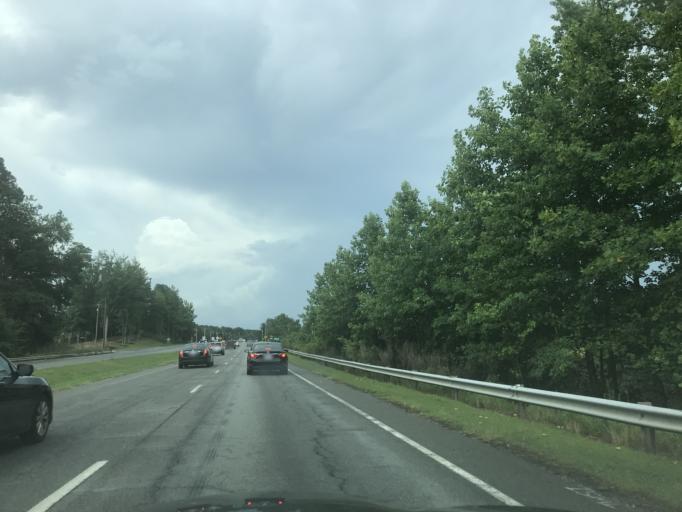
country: US
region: North Carolina
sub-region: Johnston County
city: Clayton
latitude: 35.6586
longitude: -78.4825
